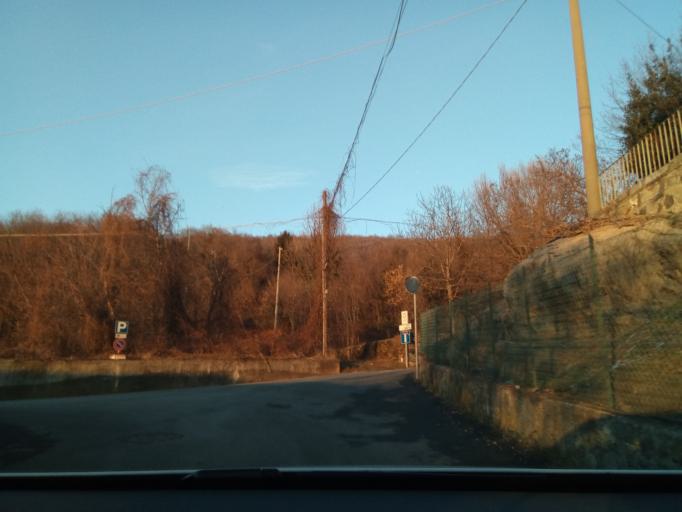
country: IT
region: Piedmont
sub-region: Provincia di Torino
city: Chiaverano
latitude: 45.4991
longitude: 7.9096
